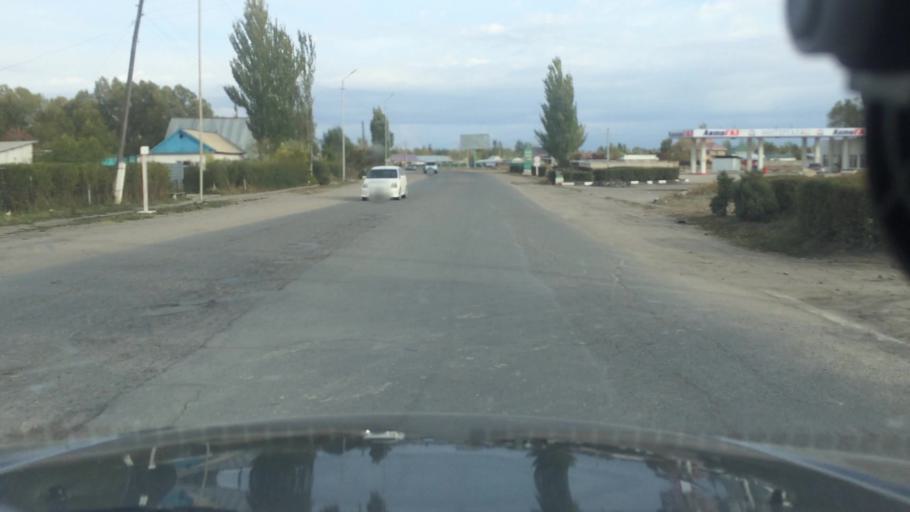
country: KG
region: Ysyk-Koel
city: Karakol
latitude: 42.5215
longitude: 78.3860
